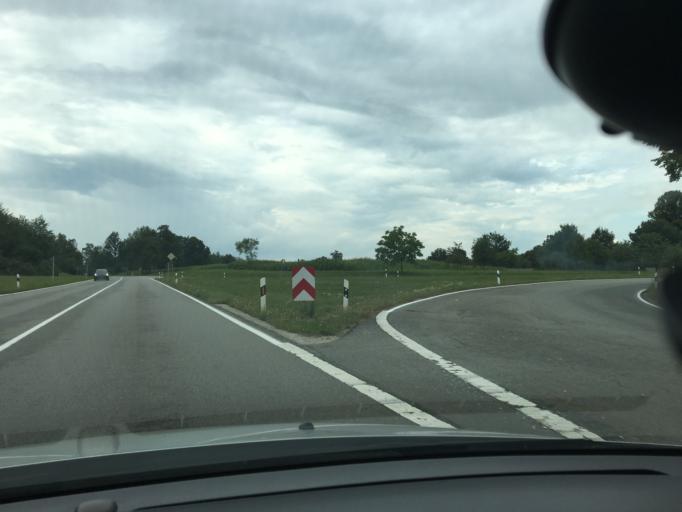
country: DE
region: Bavaria
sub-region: Upper Bavaria
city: Mettenheim
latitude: 48.2487
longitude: 12.4734
